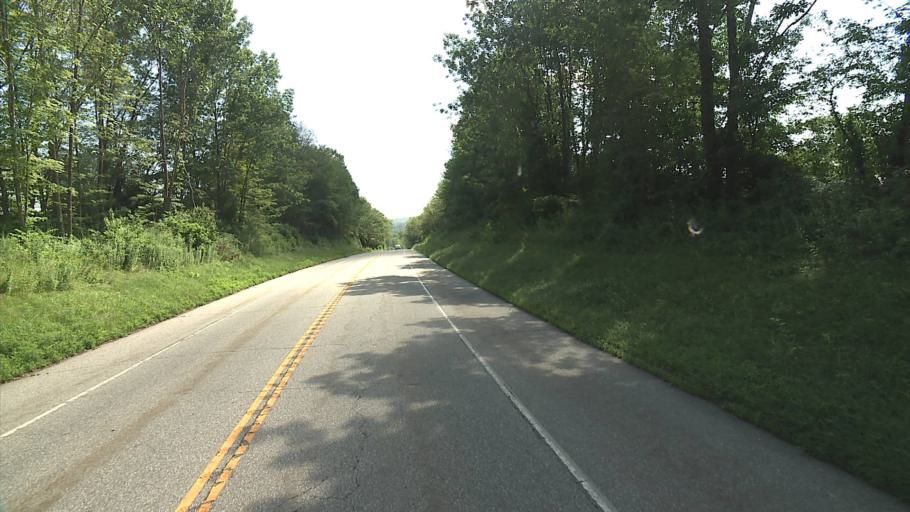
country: US
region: Connecticut
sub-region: Windham County
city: Plainfield Village
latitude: 41.7062
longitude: -71.9514
